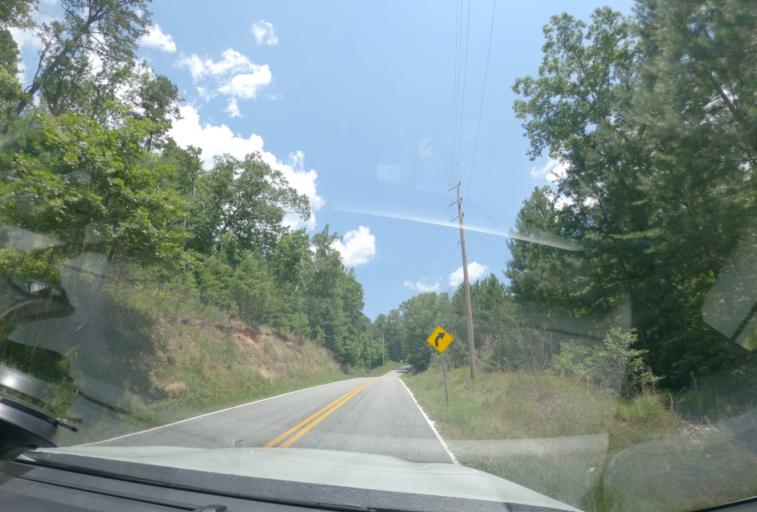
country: US
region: South Carolina
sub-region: Pickens County
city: Pickens
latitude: 34.9709
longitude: -82.8607
